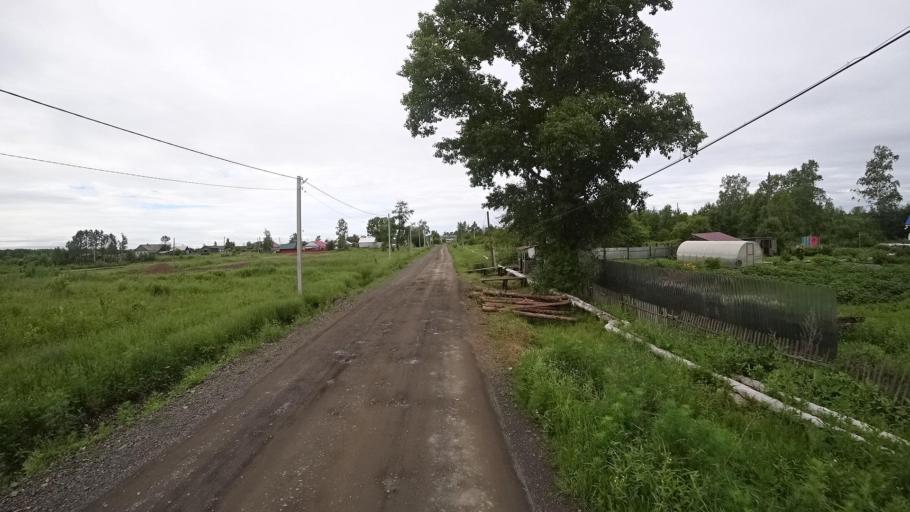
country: RU
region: Khabarovsk Krai
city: Amursk
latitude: 49.8969
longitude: 136.1346
